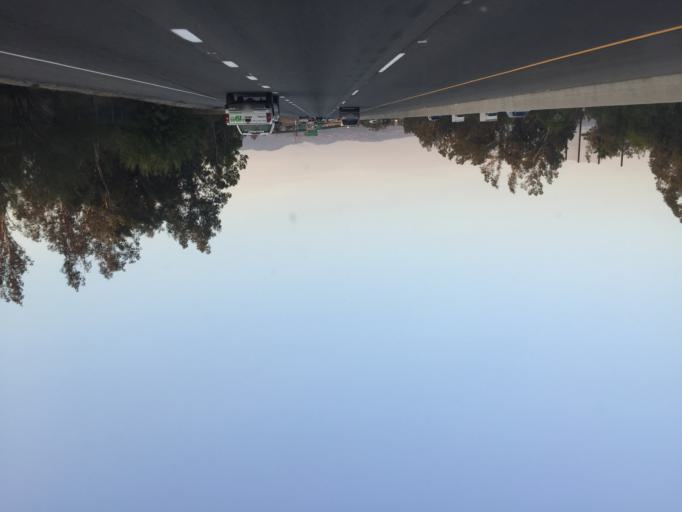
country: US
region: California
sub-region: San Bernardino County
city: Muscoy
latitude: 34.1530
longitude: -117.3245
